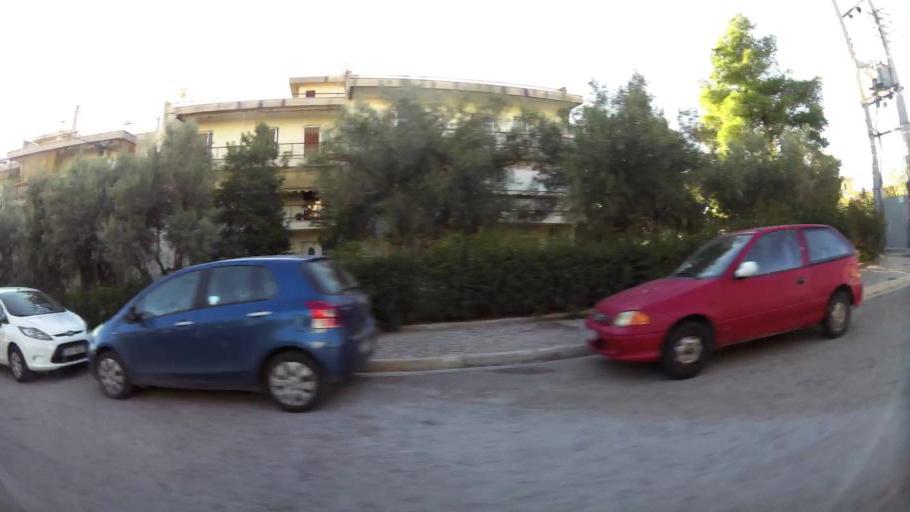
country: GR
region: Attica
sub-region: Nomarchia Anatolikis Attikis
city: Acharnes
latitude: 38.0853
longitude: 23.7208
